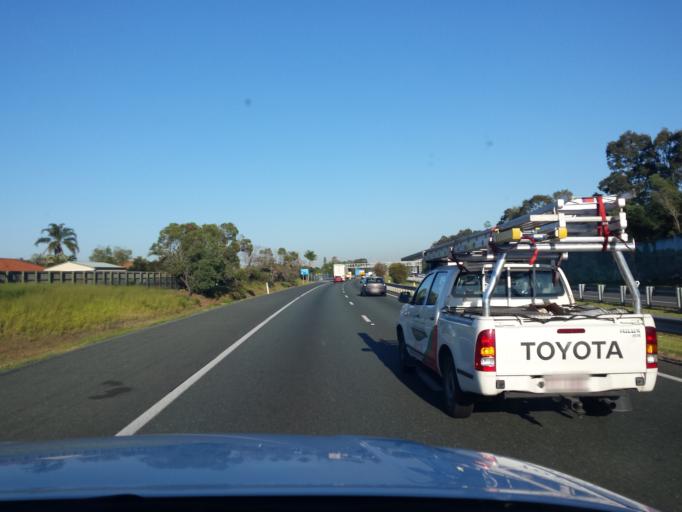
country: AU
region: Queensland
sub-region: Logan
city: Slacks Creek
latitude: -27.6671
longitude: 153.1537
